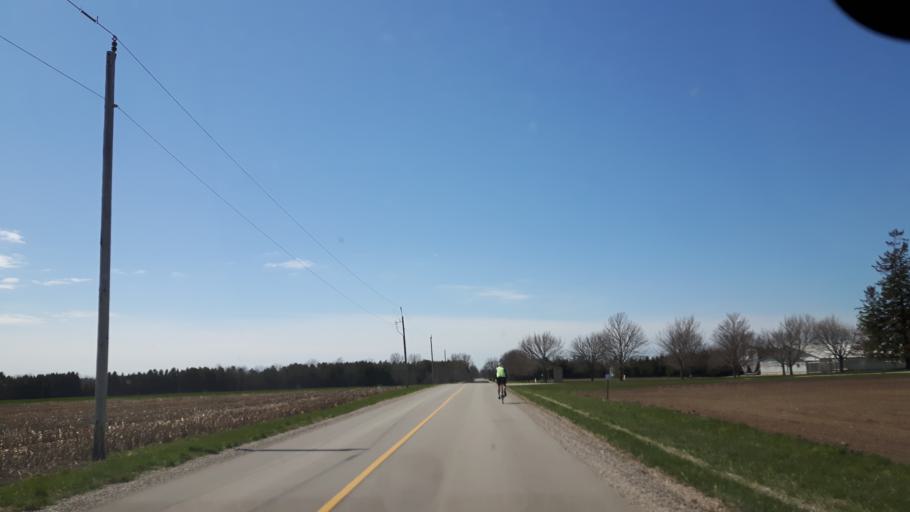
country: CA
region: Ontario
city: Bluewater
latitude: 43.5785
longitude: -81.6471
